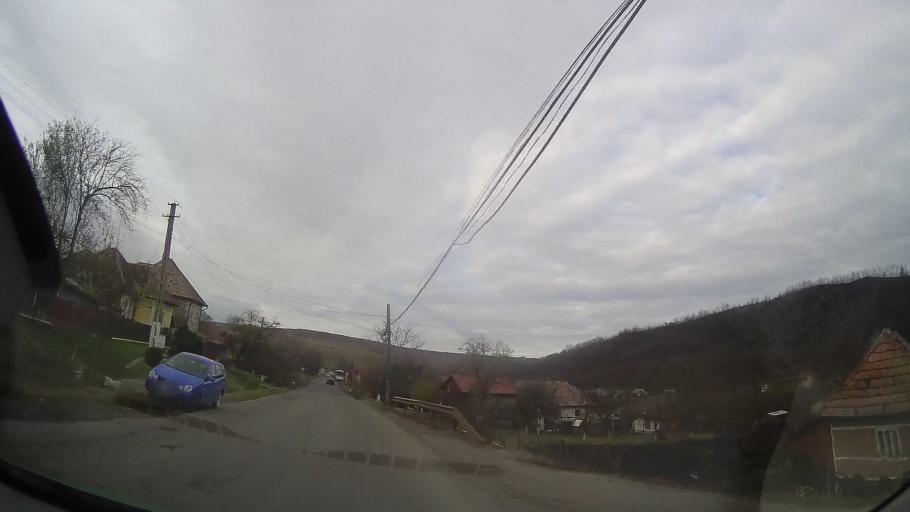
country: RO
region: Bistrita-Nasaud
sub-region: Comuna Silvasu de Campie
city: Silvasu de Campie
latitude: 46.7821
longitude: 24.2936
